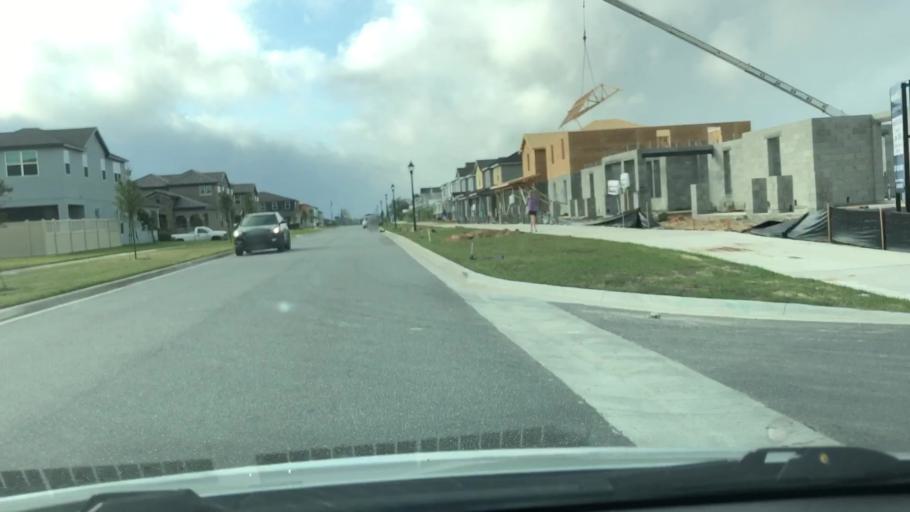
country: US
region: Florida
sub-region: Polk County
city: Citrus Ridge
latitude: 28.4338
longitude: -81.6238
